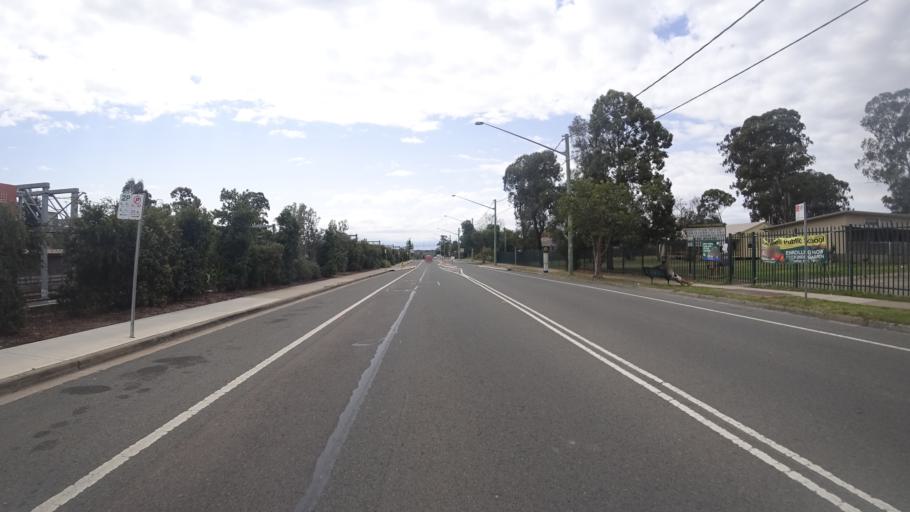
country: AU
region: New South Wales
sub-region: Campbelltown Municipality
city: Glenfield
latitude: -33.9706
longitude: 150.8953
